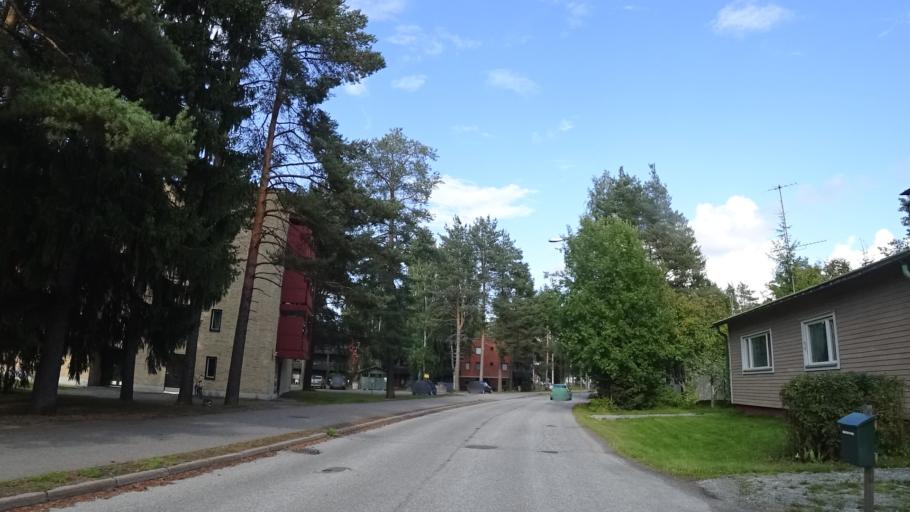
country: FI
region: North Karelia
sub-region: Pielisen Karjala
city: Lieksa
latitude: 63.3238
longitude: 30.0125
